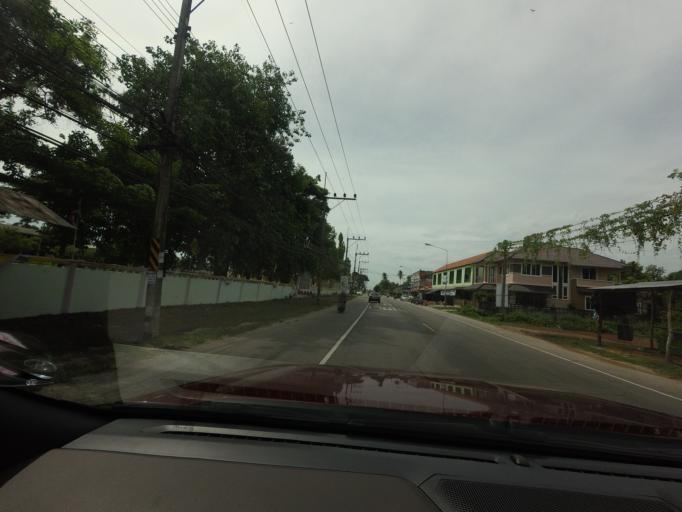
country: TH
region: Narathiwat
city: Tak Bai
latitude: 6.2411
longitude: 102.0786
